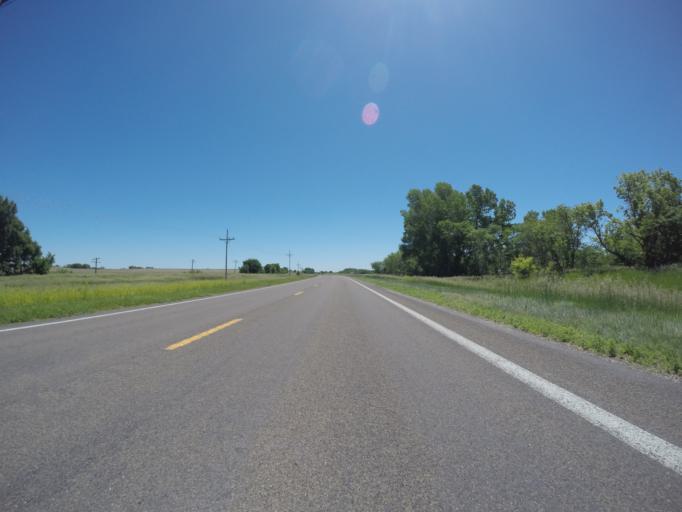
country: US
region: Kansas
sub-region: Phillips County
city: Phillipsburg
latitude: 39.8078
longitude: -99.4948
